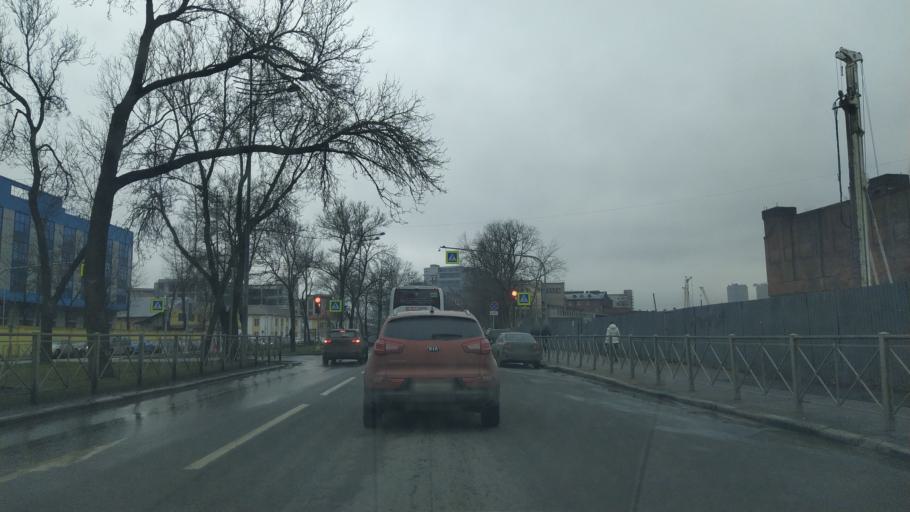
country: RU
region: St.-Petersburg
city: Centralniy
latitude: 59.8968
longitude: 30.3338
